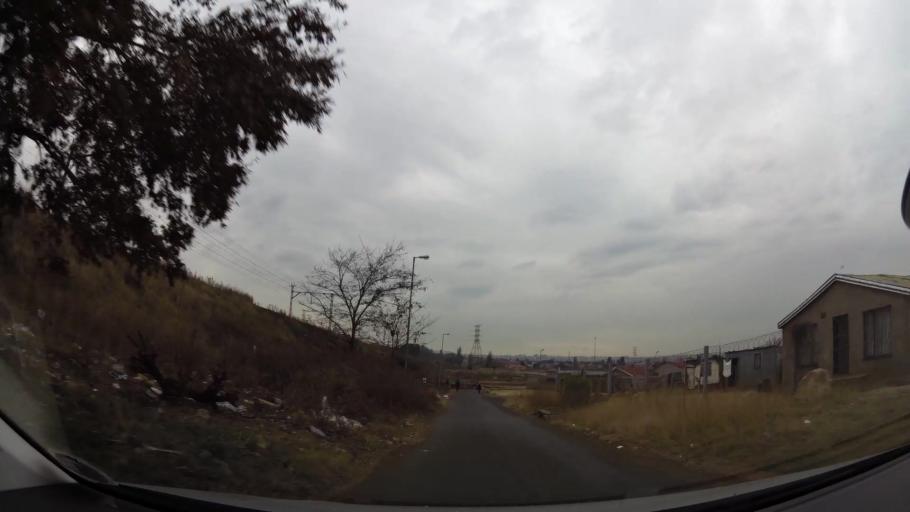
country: ZA
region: Gauteng
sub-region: City of Johannesburg Metropolitan Municipality
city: Soweto
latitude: -26.2410
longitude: 27.8700
